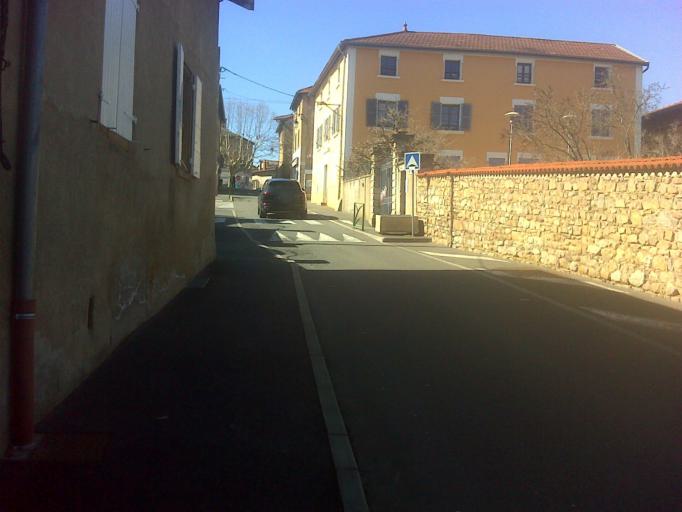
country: FR
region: Rhone-Alpes
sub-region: Departement du Rhone
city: Lentilly
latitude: 45.8196
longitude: 4.6639
